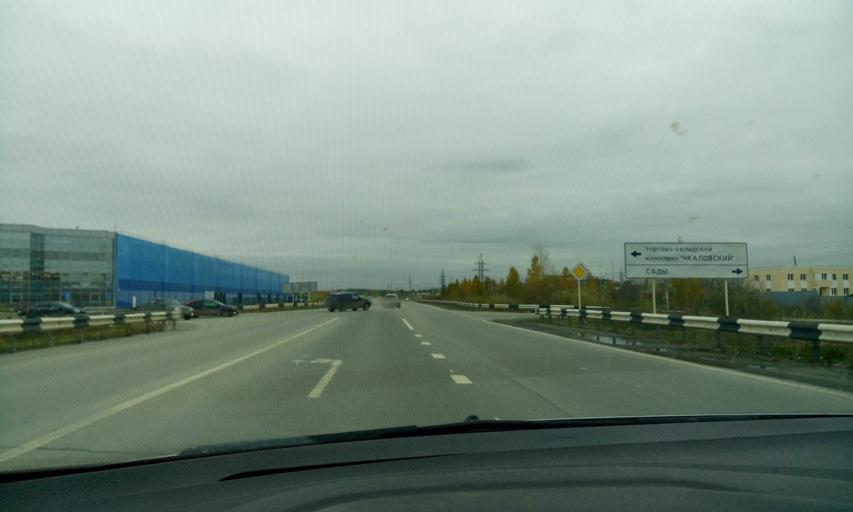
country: RU
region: Sverdlovsk
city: Istok
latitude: 56.7654
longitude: 60.7412
